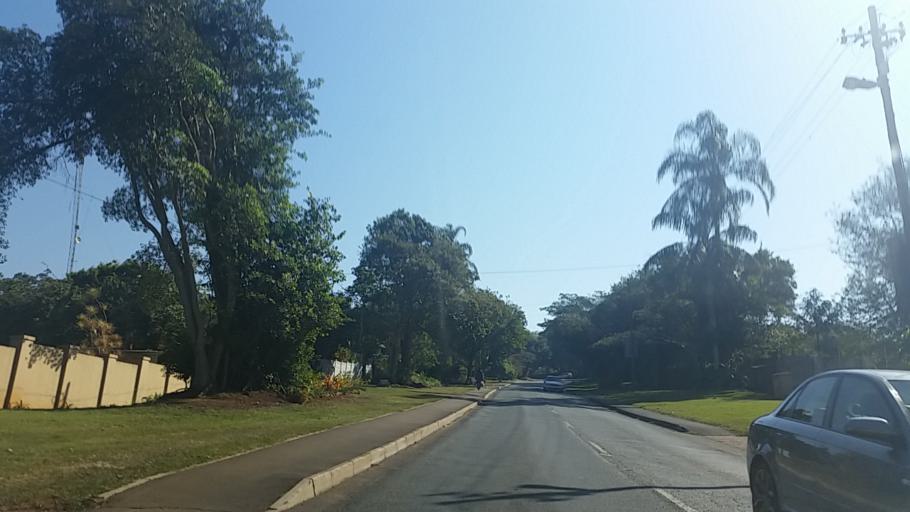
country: ZA
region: KwaZulu-Natal
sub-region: eThekwini Metropolitan Municipality
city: Berea
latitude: -29.8299
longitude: 30.8967
